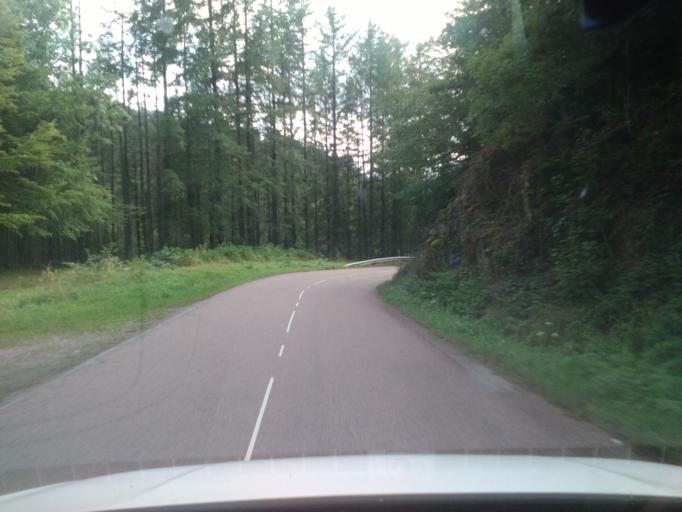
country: FR
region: Lorraine
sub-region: Departement des Vosges
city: Senones
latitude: 48.3374
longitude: 6.9984
